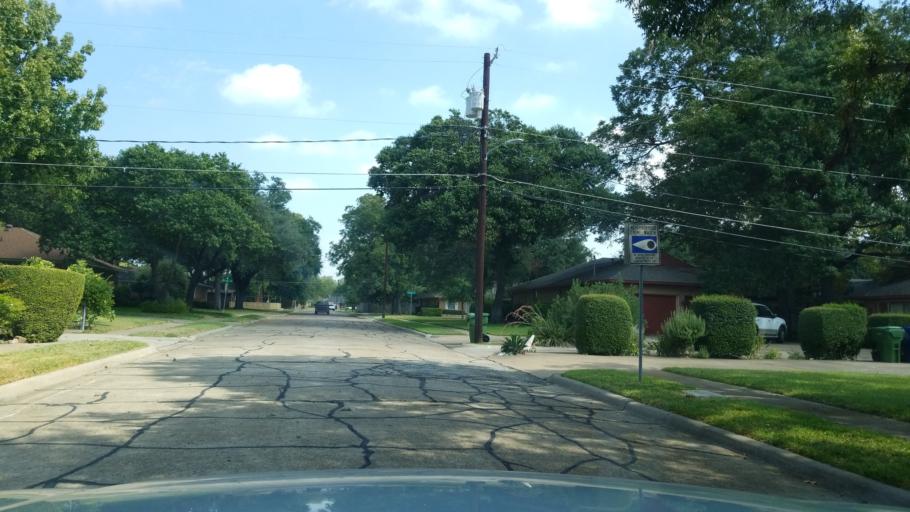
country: US
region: Texas
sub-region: Dallas County
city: Garland
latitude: 32.8958
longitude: -96.6634
